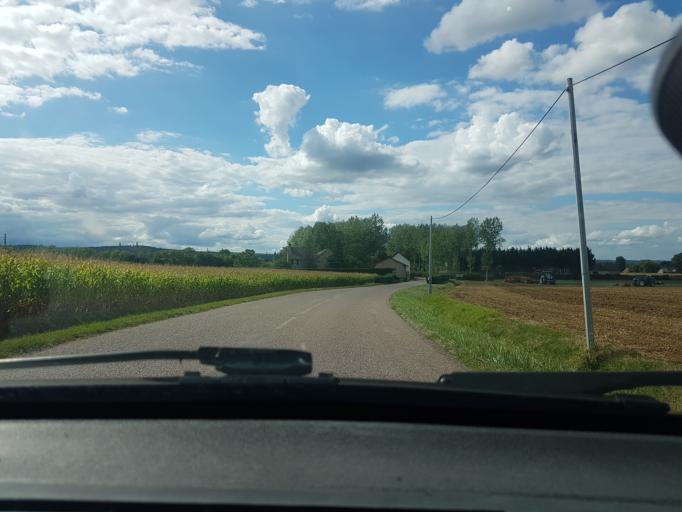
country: FR
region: Bourgogne
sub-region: Departement de Saone-et-Loire
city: Fontaines
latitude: 46.8445
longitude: 4.7843
